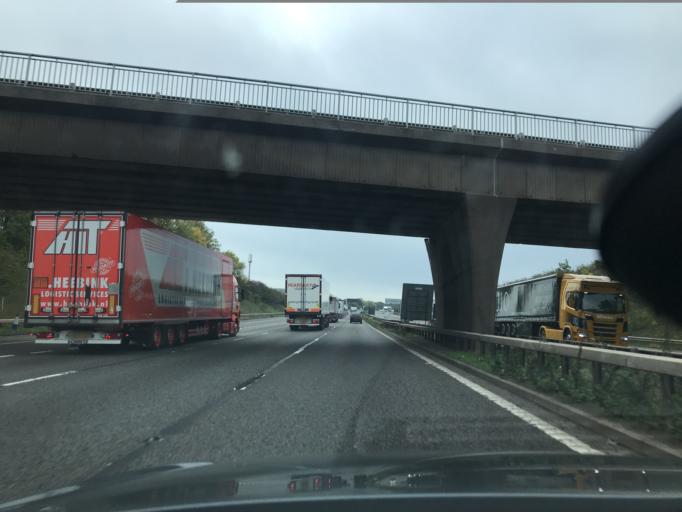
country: GB
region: England
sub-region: Staffordshire
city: Stafford
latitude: 52.8116
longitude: -2.1549
